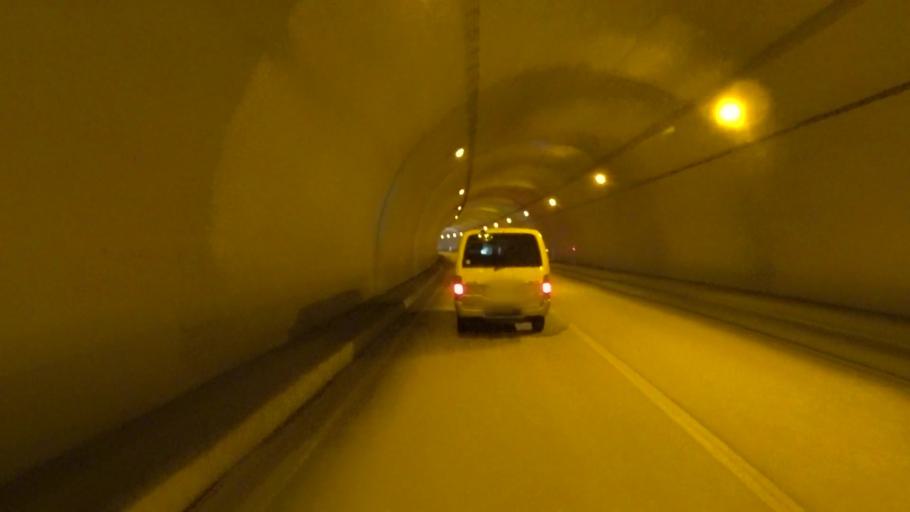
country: JP
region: Kyoto
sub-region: Kyoto-shi
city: Kamigyo-ku
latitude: 35.2515
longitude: 135.6364
